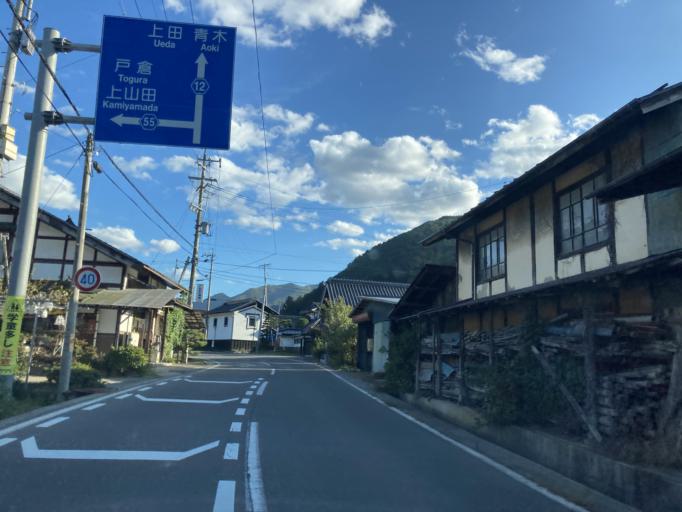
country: JP
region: Nagano
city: Omachi
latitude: 36.4497
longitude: 138.0657
